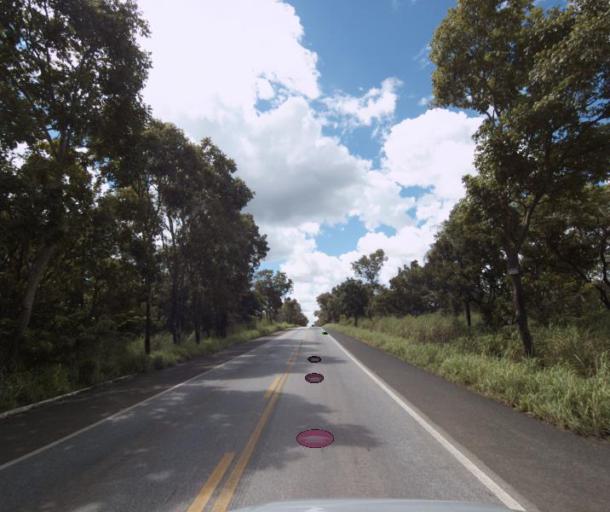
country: BR
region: Goias
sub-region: Porangatu
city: Porangatu
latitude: -13.8116
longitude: -49.0393
